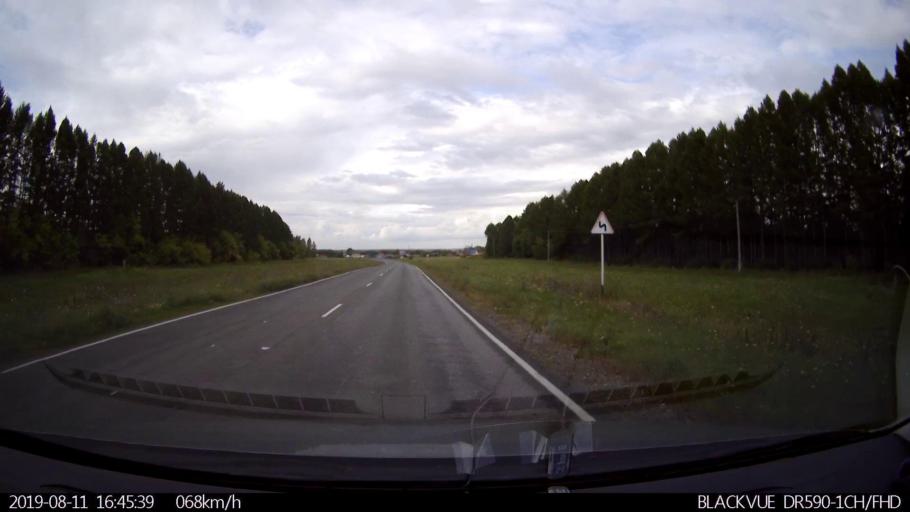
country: RU
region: Ulyanovsk
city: Mayna
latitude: 54.1920
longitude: 47.6873
